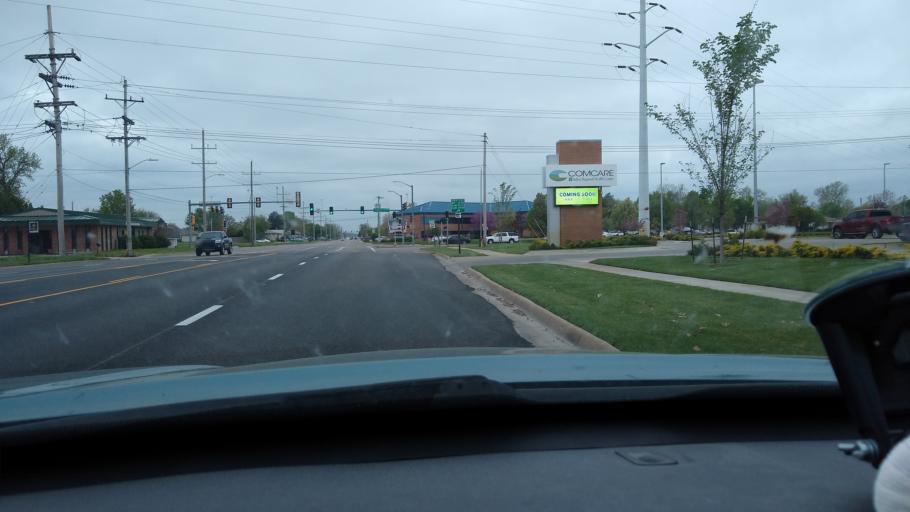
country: US
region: Kansas
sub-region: Saline County
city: Salina
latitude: 38.8058
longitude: -97.5944
